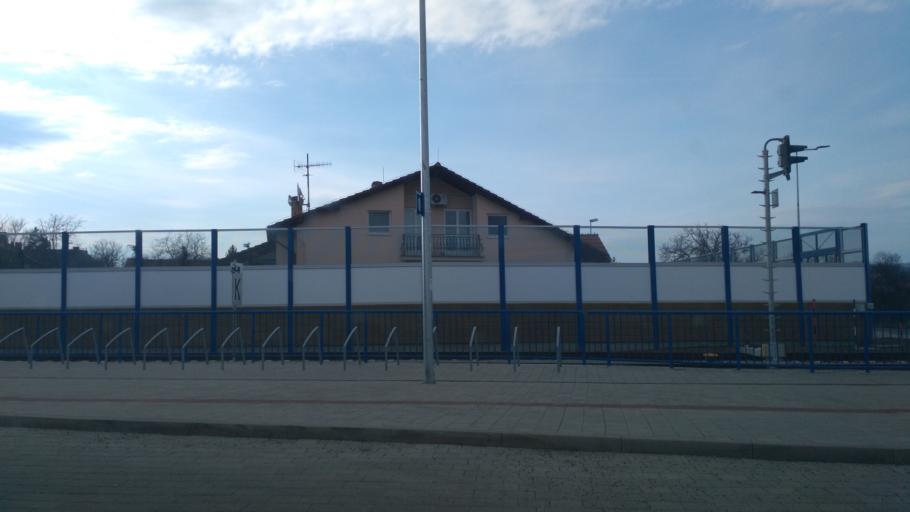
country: SK
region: Kosicky
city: Moldava nad Bodvou
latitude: 48.6089
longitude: 21.0042
